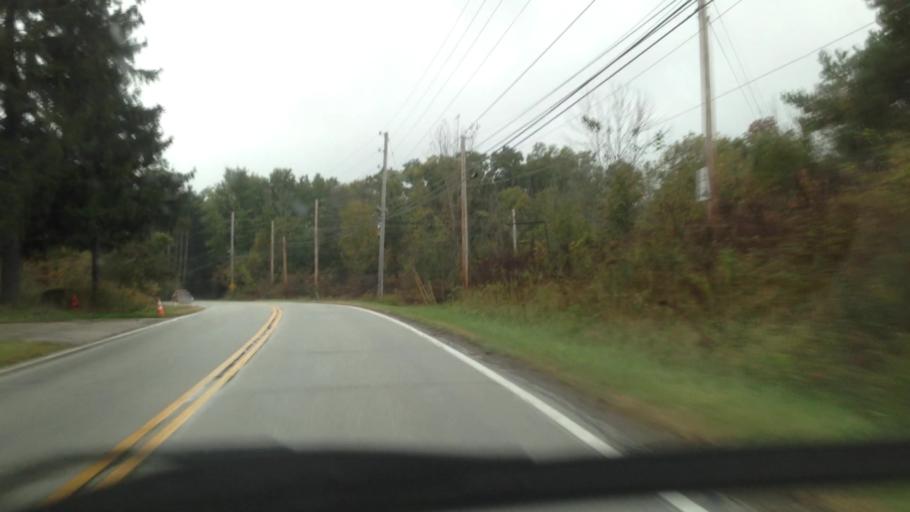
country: US
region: Ohio
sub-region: Summit County
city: Boston Heights
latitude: 41.2620
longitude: -81.4828
